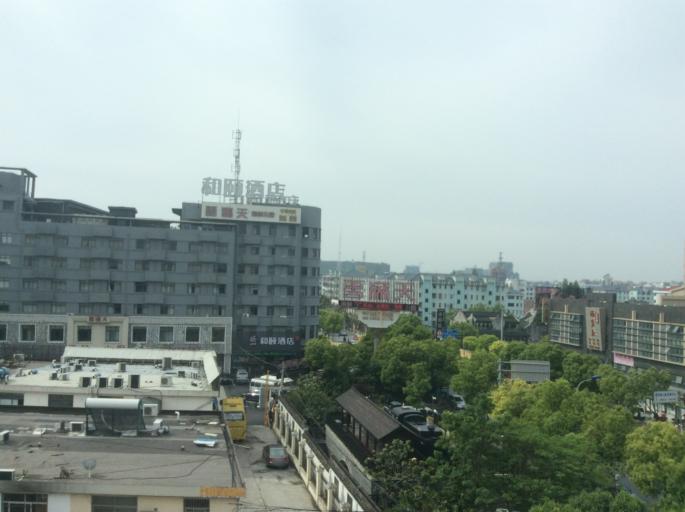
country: CN
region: Shanghai Shi
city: Kangqiao
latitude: 31.2021
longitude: 121.6985
